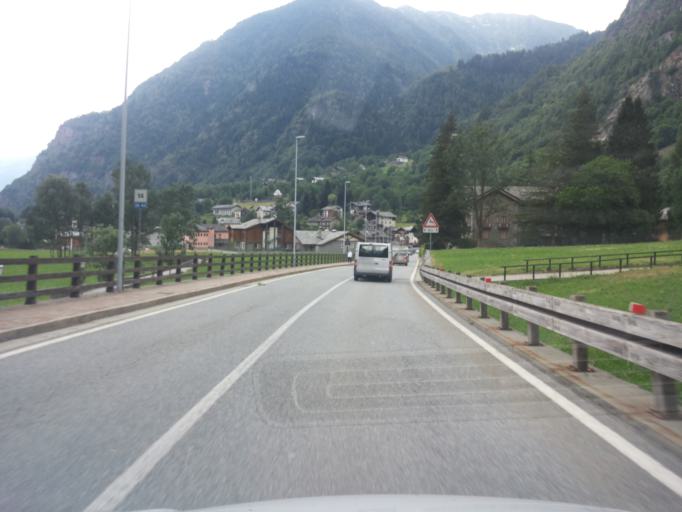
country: IT
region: Aosta Valley
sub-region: Valle d'Aosta
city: Issime
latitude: 45.6897
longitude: 7.8556
